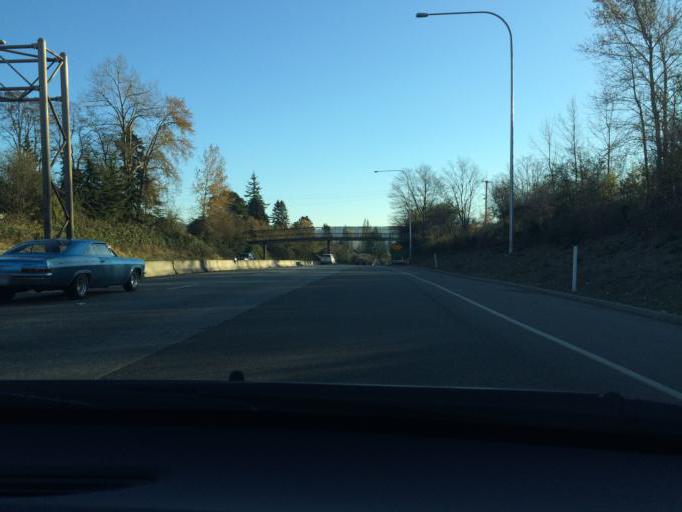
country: US
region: Washington
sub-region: Whatcom County
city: Bellingham
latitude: 48.7693
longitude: -122.4629
